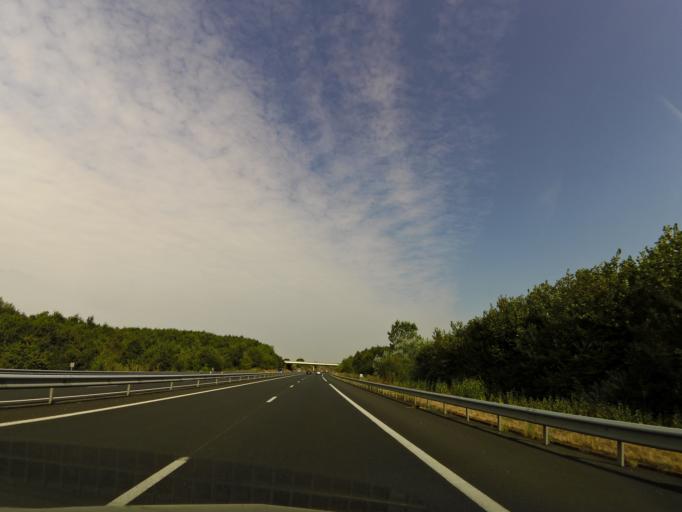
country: FR
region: Pays de la Loire
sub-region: Departement de la Vendee
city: Les Brouzils
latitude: 46.9056
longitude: -1.3147
